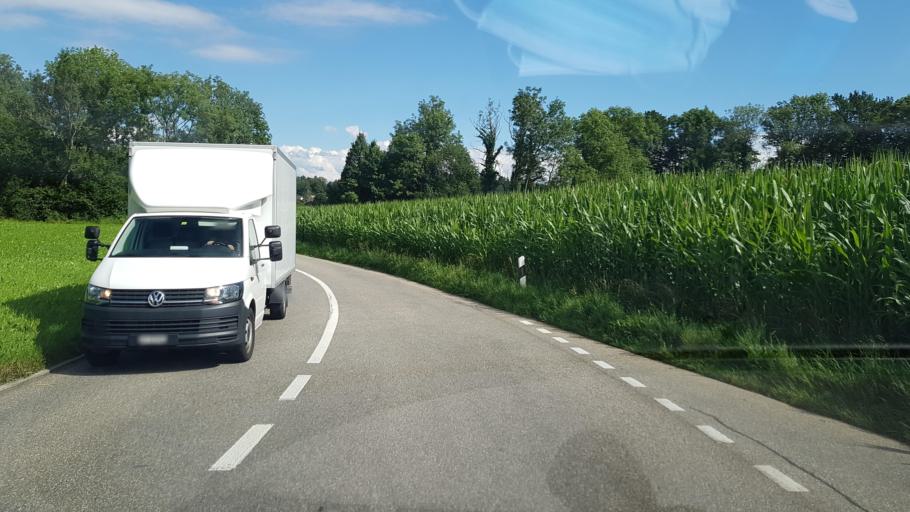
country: CH
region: Solothurn
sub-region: Bezirk Lebern
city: Riedholz
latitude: 47.2459
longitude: 7.5814
